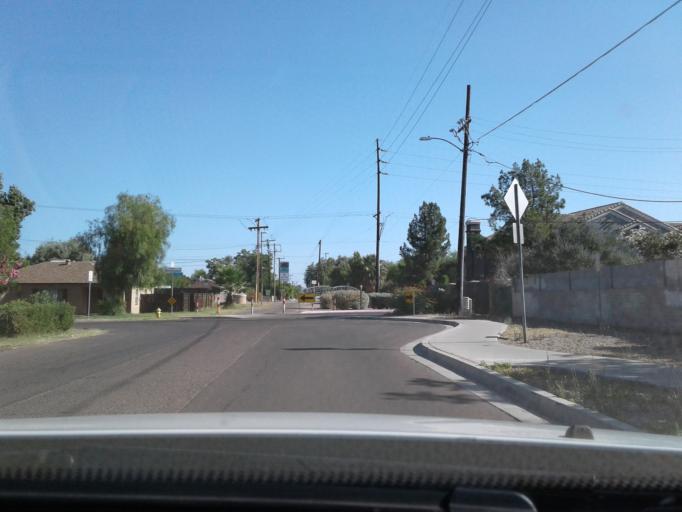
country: US
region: Arizona
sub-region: Maricopa County
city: Phoenix
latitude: 33.5027
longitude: -112.0781
